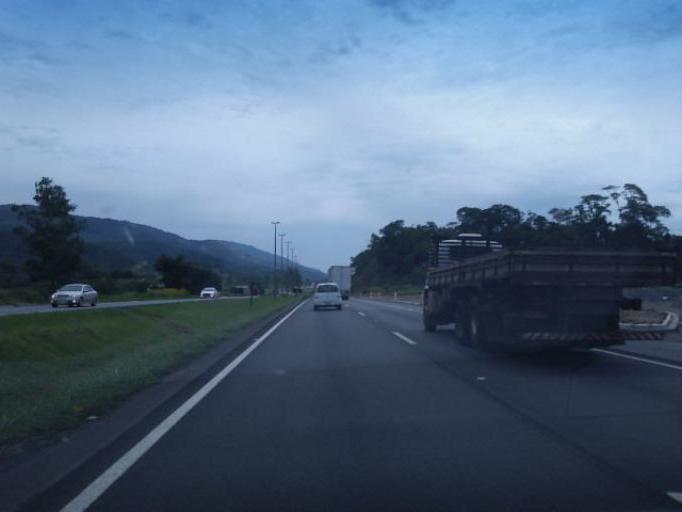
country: BR
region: Sao Paulo
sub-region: Miracatu
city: Miracatu
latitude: -24.2667
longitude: -47.3919
